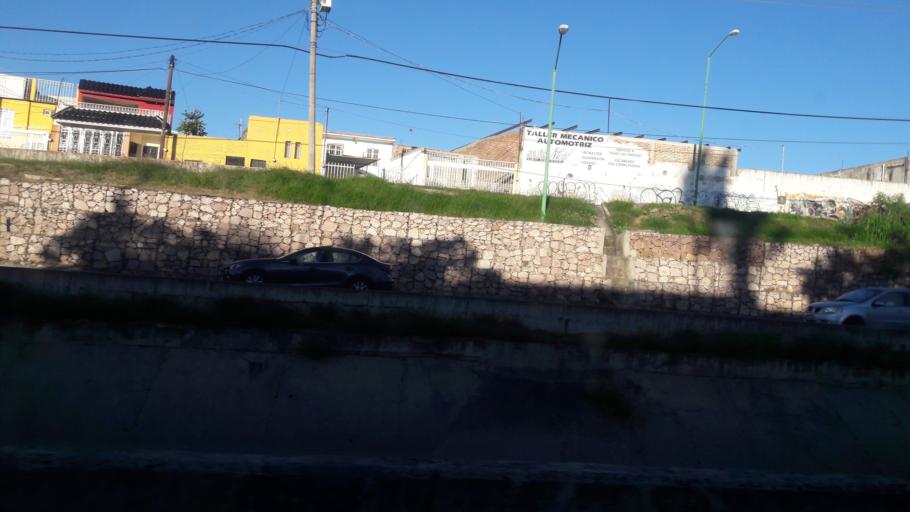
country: MX
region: Guanajuato
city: Leon
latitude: 21.1337
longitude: -101.6784
